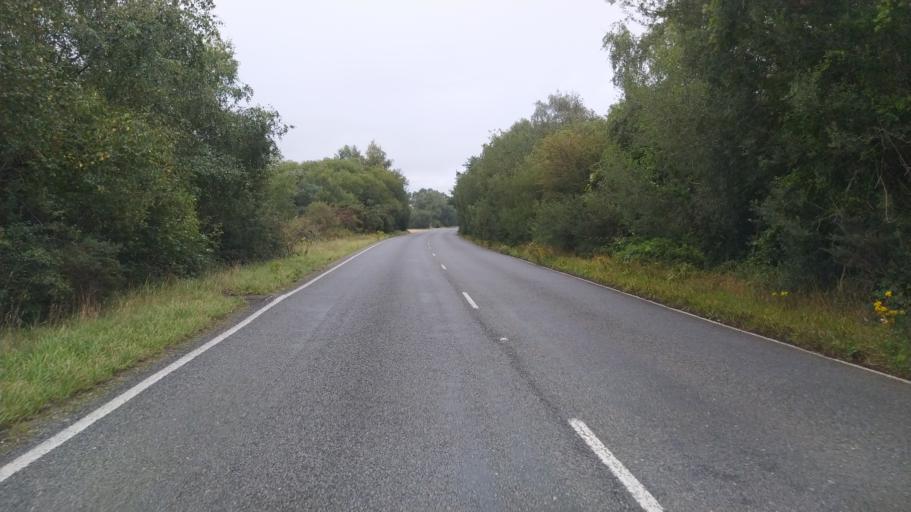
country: GB
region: England
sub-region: Hampshire
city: Sway
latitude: 50.8264
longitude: -1.6507
